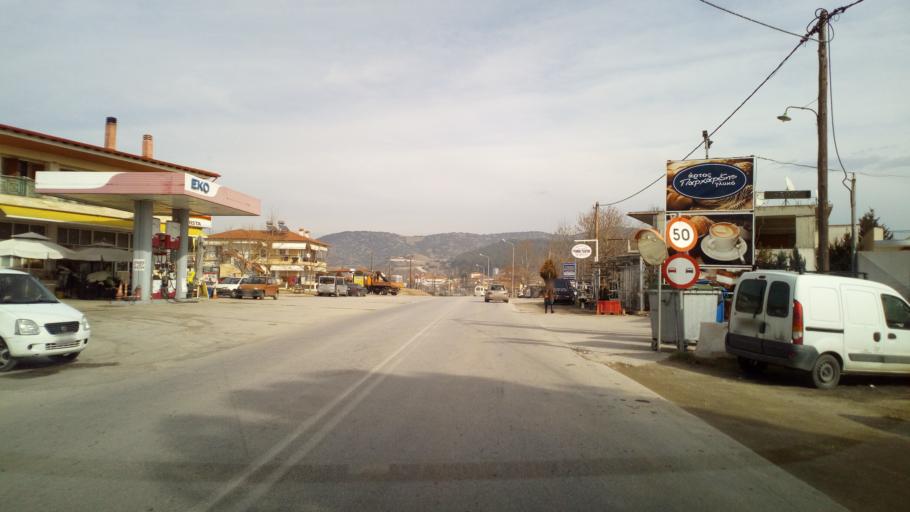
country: GR
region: Central Macedonia
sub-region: Nomos Thessalonikis
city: Kolchikon
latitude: 40.7556
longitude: 23.1272
